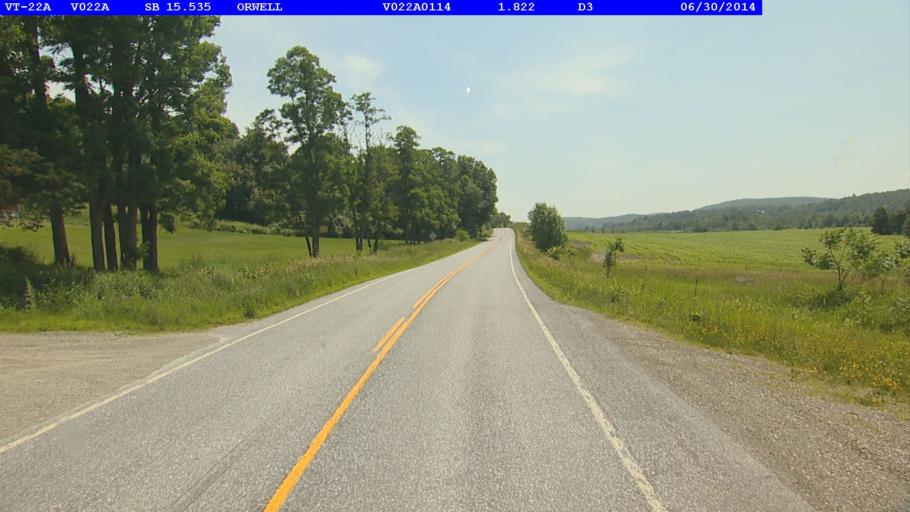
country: US
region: New York
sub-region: Essex County
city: Ticonderoga
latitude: 43.7832
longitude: -73.3070
